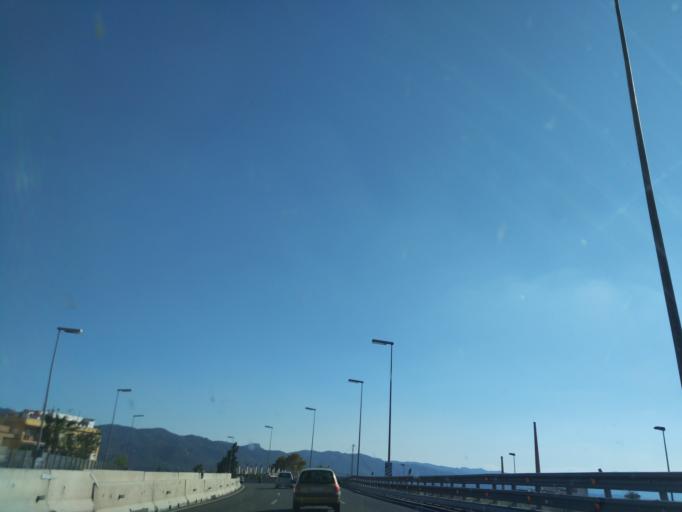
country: ES
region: Murcia
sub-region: Murcia
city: Murcia
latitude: 37.9715
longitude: -1.1382
